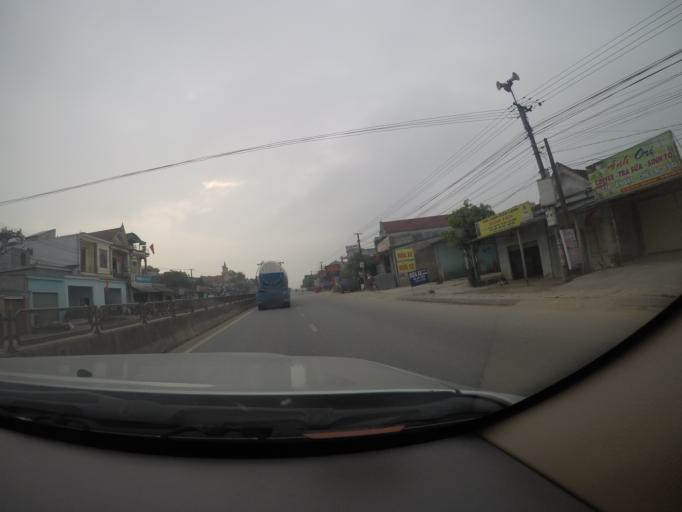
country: VN
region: Ha Tinh
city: Cam Xuyen
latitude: 18.1990
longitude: 106.1654
